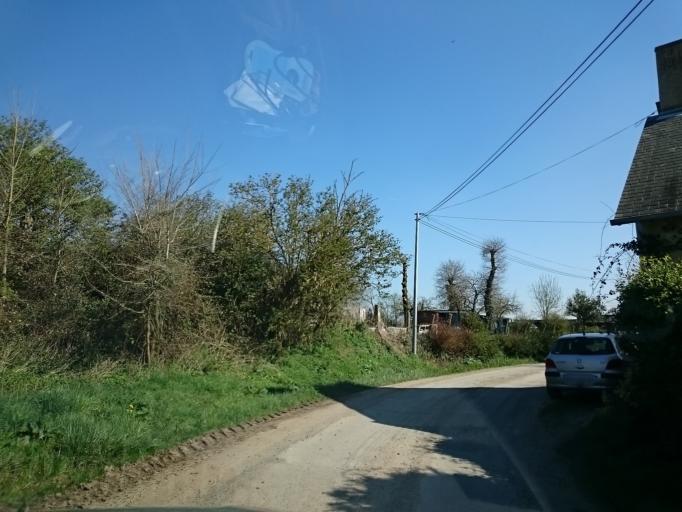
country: FR
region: Brittany
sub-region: Departement d'Ille-et-Vilaine
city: Orgeres
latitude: 48.0144
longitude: -1.6869
